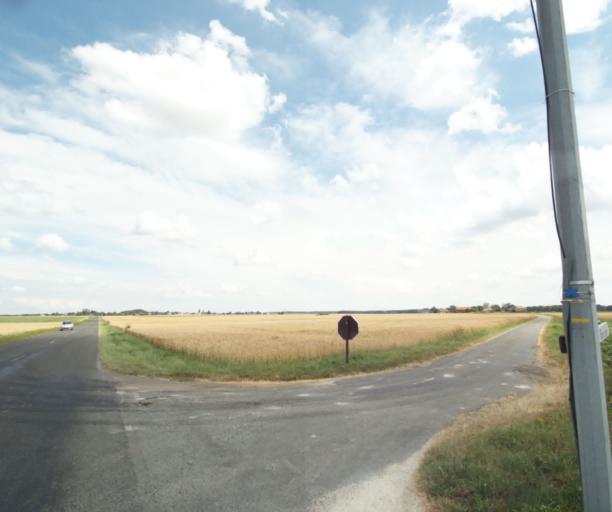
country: FR
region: Ile-de-France
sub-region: Departement de Seine-et-Marne
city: Hericy
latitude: 48.4500
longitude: 2.8074
